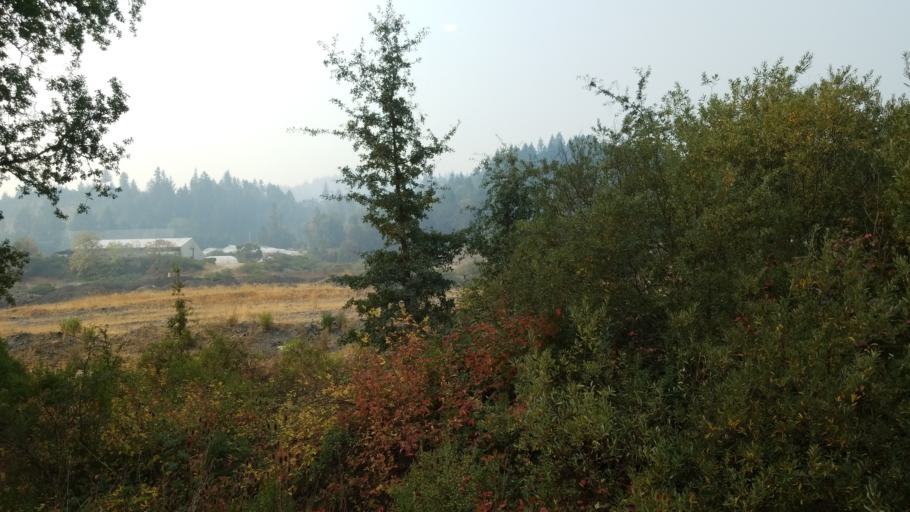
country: US
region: California
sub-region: Mendocino County
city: Willits
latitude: 39.4029
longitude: -123.3662
